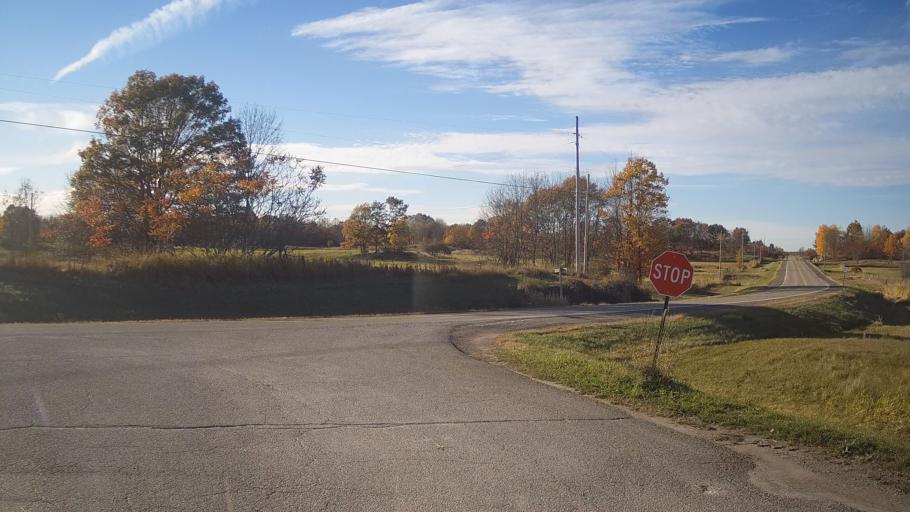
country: CA
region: Ontario
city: Perth
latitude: 44.7065
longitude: -76.4302
